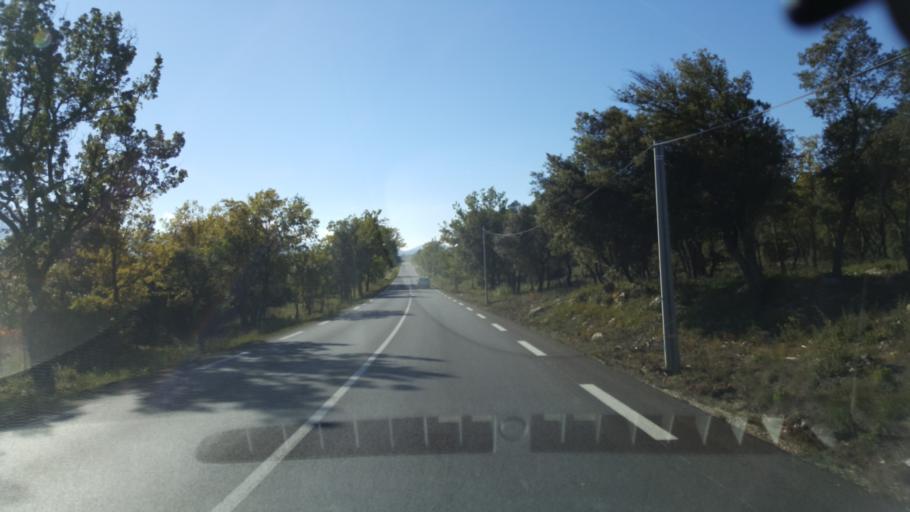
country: FR
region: Provence-Alpes-Cote d'Azur
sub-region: Departement du Var
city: Rougiers
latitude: 43.4219
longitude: 5.8387
